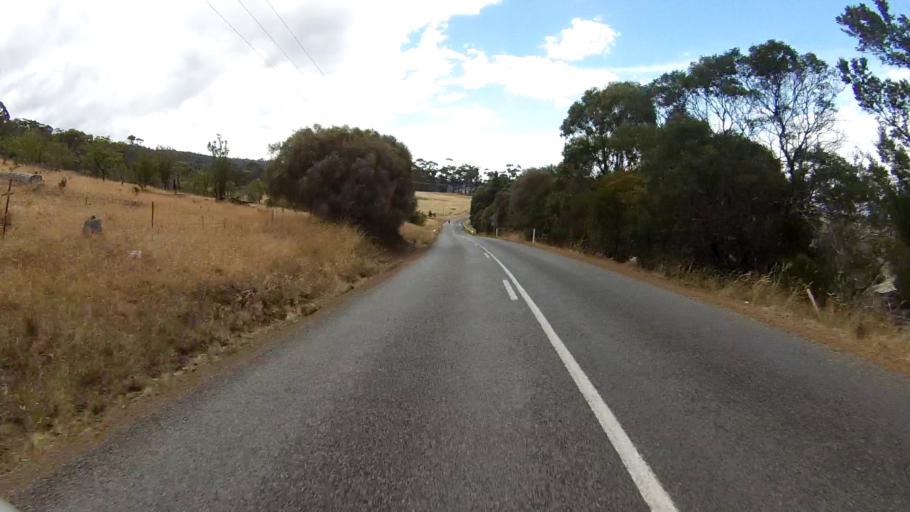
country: AU
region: Tasmania
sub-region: Sorell
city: Sorell
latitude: -42.2175
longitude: 148.0304
